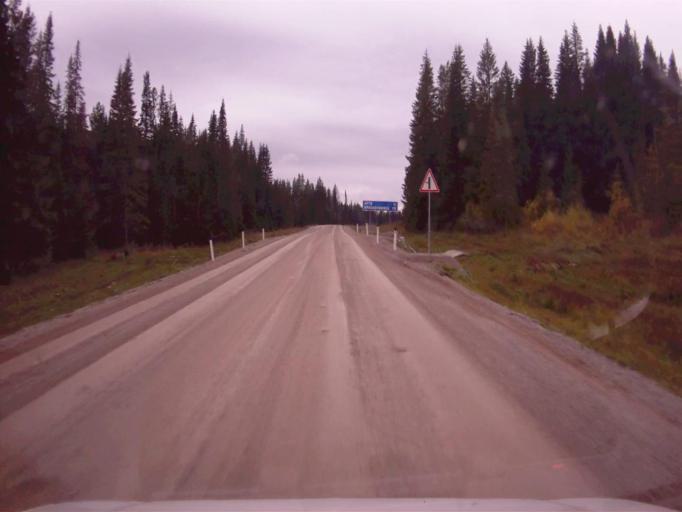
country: RU
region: Chelyabinsk
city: Nyazepetrovsk
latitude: 56.0578
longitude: 59.5562
